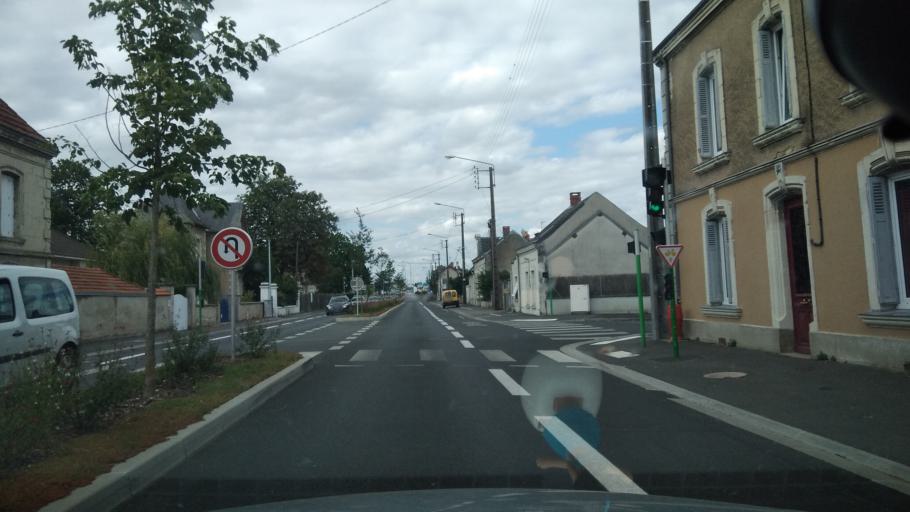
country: FR
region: Poitou-Charentes
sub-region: Departement de la Vienne
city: Antran
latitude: 46.8321
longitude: 0.5462
